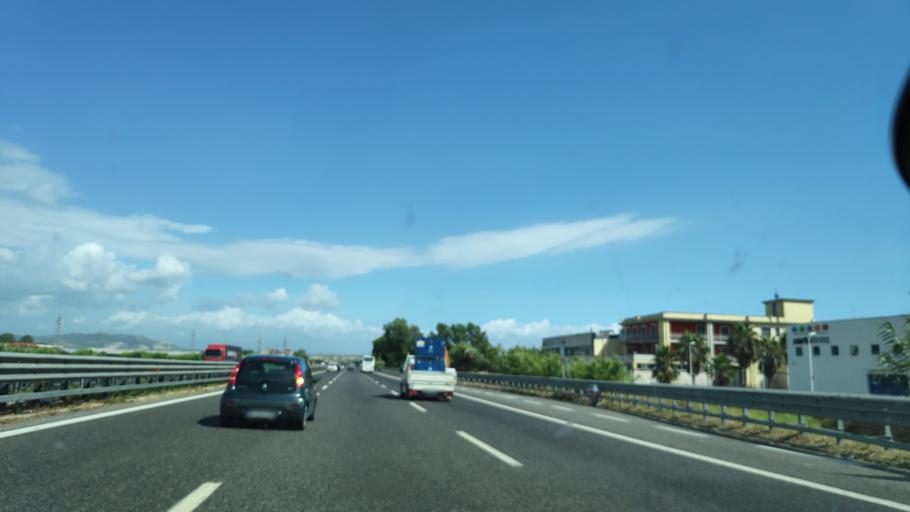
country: IT
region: Campania
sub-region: Provincia di Salerno
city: Sant'Antonio
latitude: 40.6420
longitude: 14.8978
